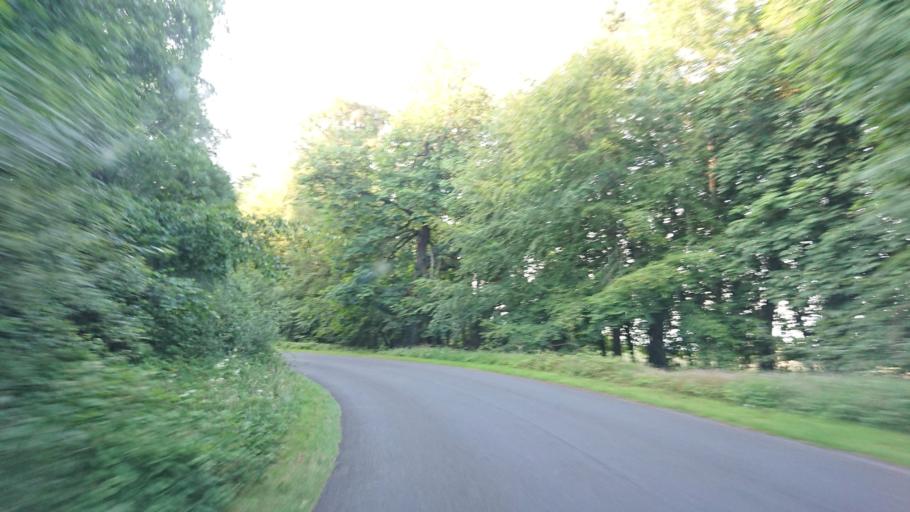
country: IE
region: Connaught
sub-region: Roscommon
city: Boyle
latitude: 53.9758
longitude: -8.2416
